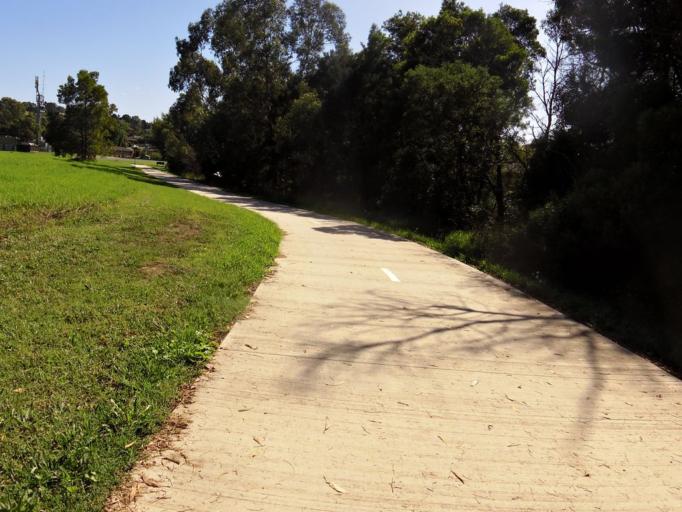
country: AU
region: Victoria
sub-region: Yarra Ranges
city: Kilsyth
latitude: -37.7876
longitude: 145.3203
